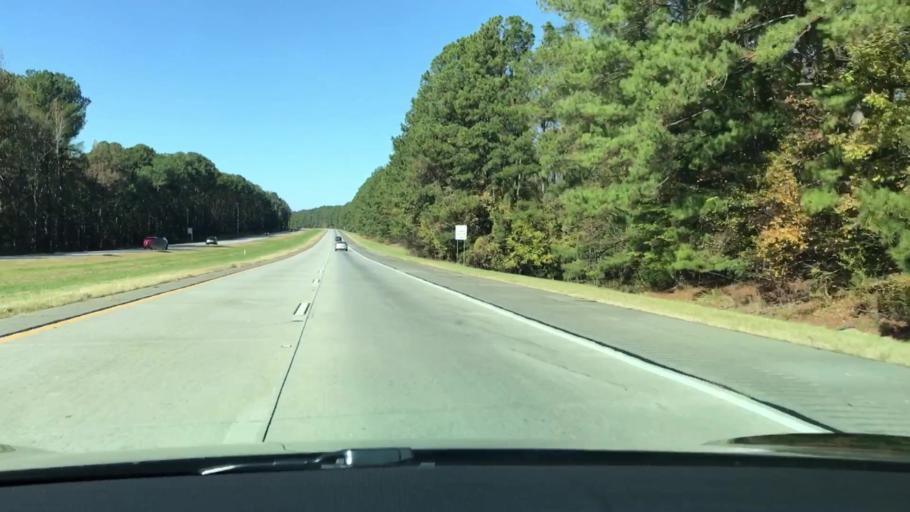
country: US
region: Georgia
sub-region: Taliaferro County
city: Crawfordville
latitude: 33.5198
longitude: -82.8657
